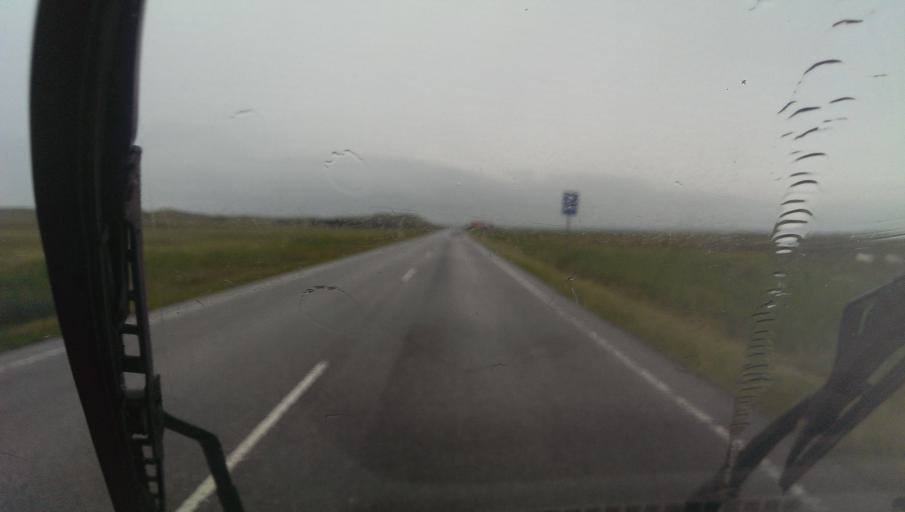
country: DK
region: Central Jutland
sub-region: Ringkobing-Skjern Kommune
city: Ringkobing
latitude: 56.2256
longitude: 8.1399
